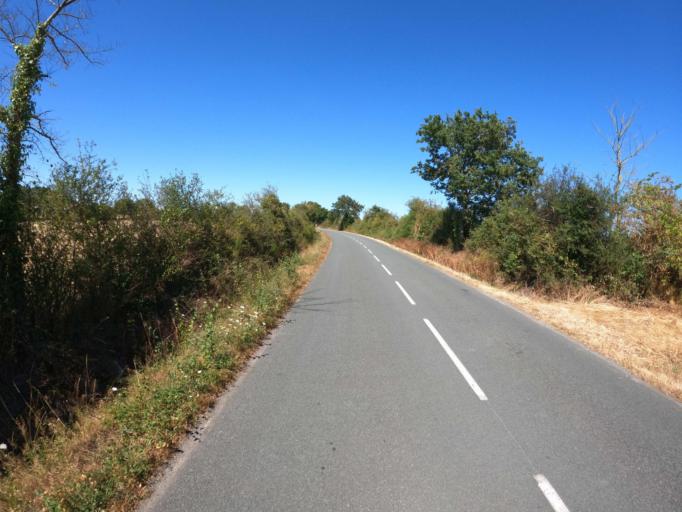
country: FR
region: Pays de la Loire
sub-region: Departement de la Vendee
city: Saint-Aubin-des-Ormeaux
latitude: 46.9817
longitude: -1.0511
